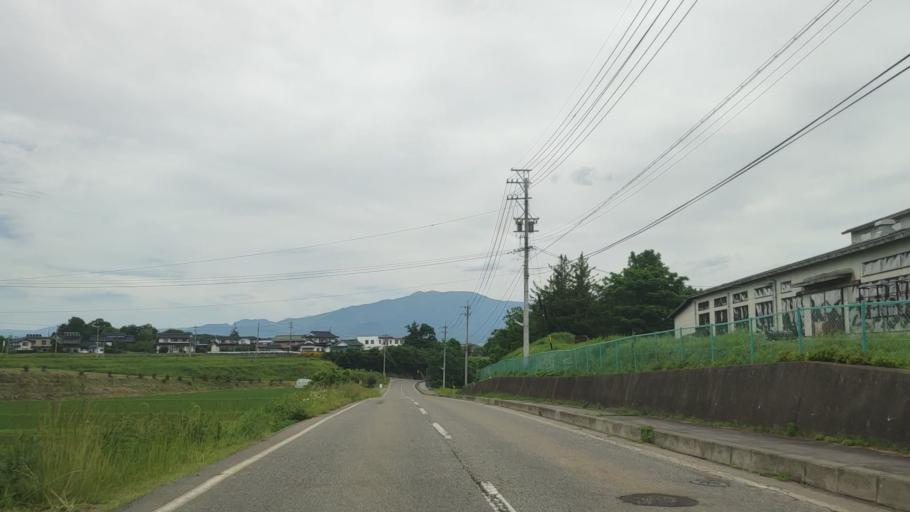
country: JP
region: Nagano
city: Kamimaruko
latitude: 36.2962
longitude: 138.3183
